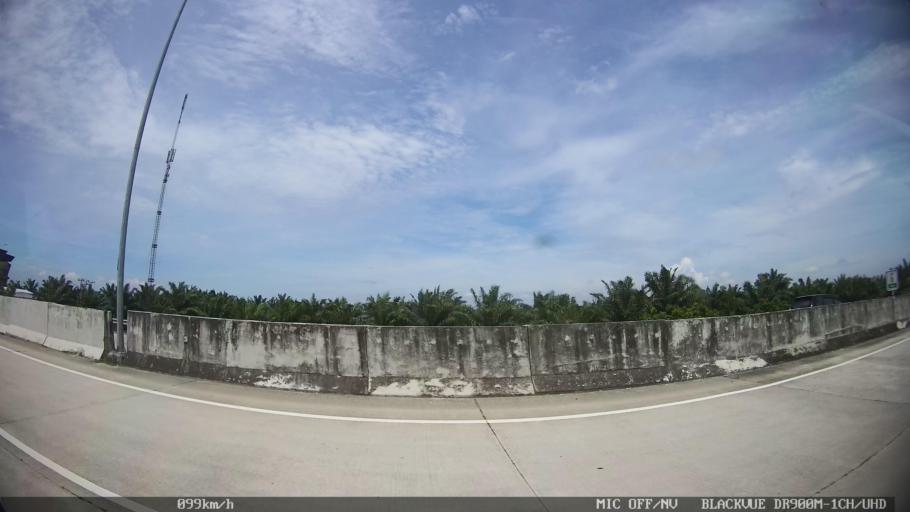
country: ID
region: North Sumatra
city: Percut
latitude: 3.5909
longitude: 98.8445
